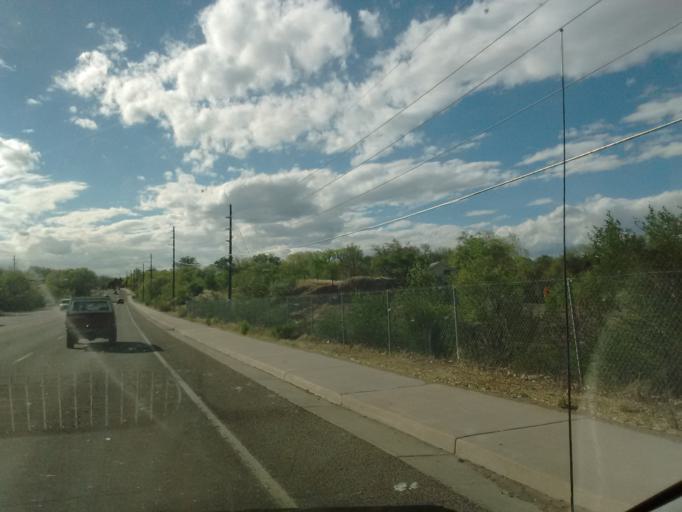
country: US
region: Colorado
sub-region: Mesa County
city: Redlands
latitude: 39.0660
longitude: -108.5997
